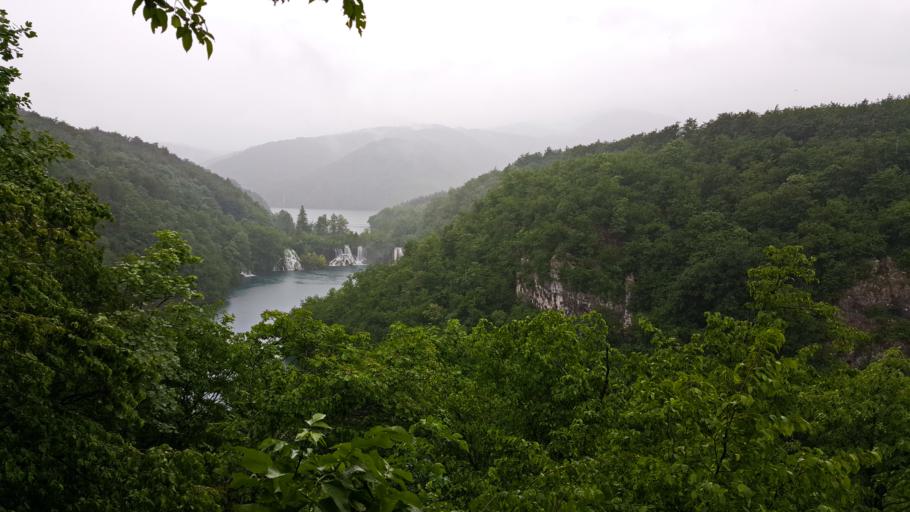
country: HR
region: Licko-Senjska
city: Jezerce
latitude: 44.8972
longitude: 15.6114
